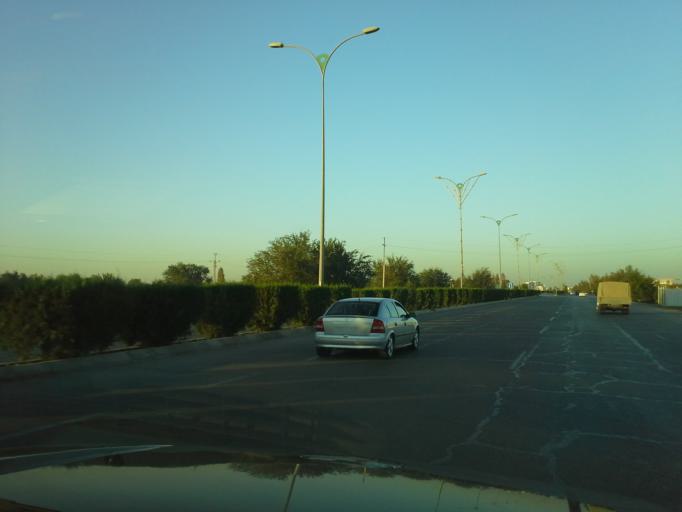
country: TM
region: Dasoguz
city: Dasoguz
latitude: 41.8090
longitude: 59.9092
